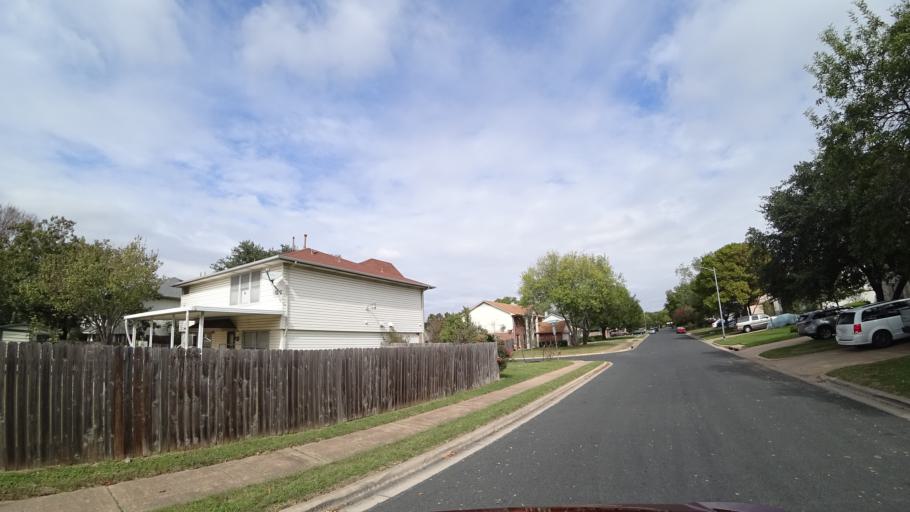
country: US
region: Texas
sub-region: Travis County
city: Wells Branch
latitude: 30.4243
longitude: -97.6935
